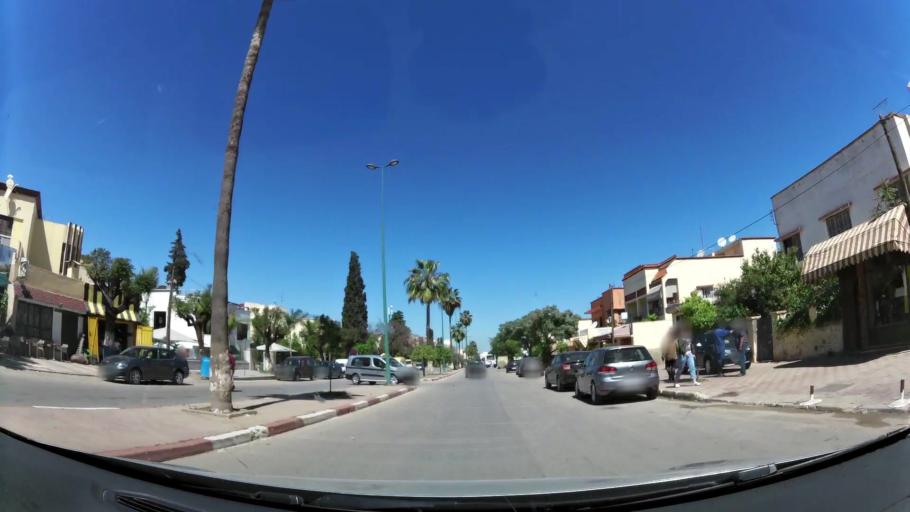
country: MA
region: Meknes-Tafilalet
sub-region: Meknes
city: Meknes
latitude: 33.9042
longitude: -5.5255
